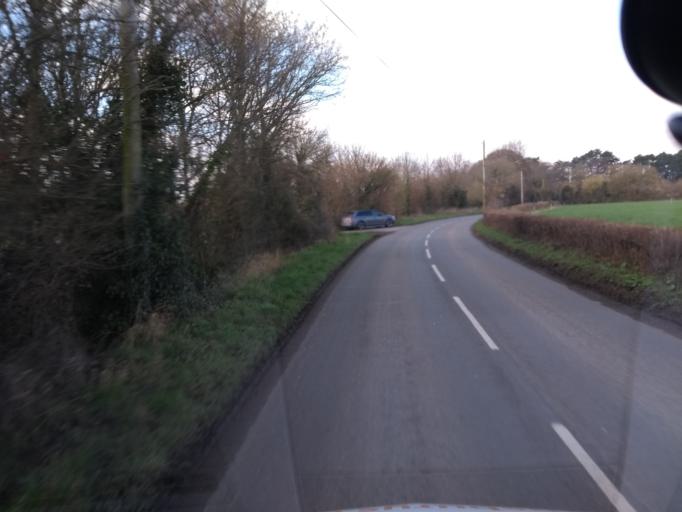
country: GB
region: England
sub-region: Somerset
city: Taunton
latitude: 50.9883
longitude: -3.0710
